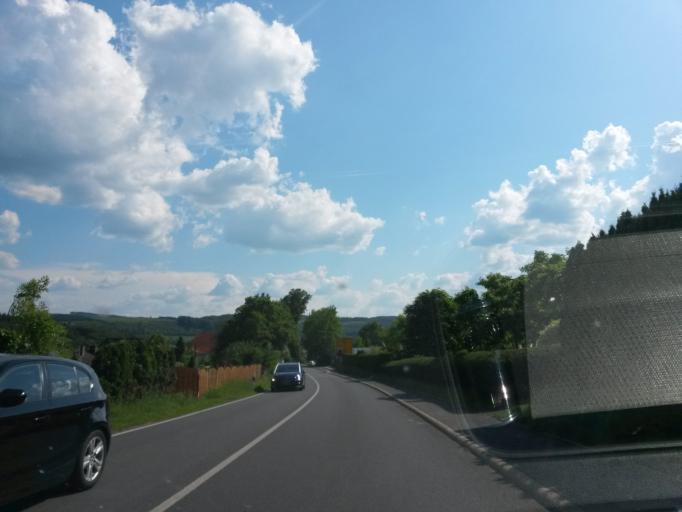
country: DE
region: North Rhine-Westphalia
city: Balve
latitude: 51.3132
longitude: 7.8778
